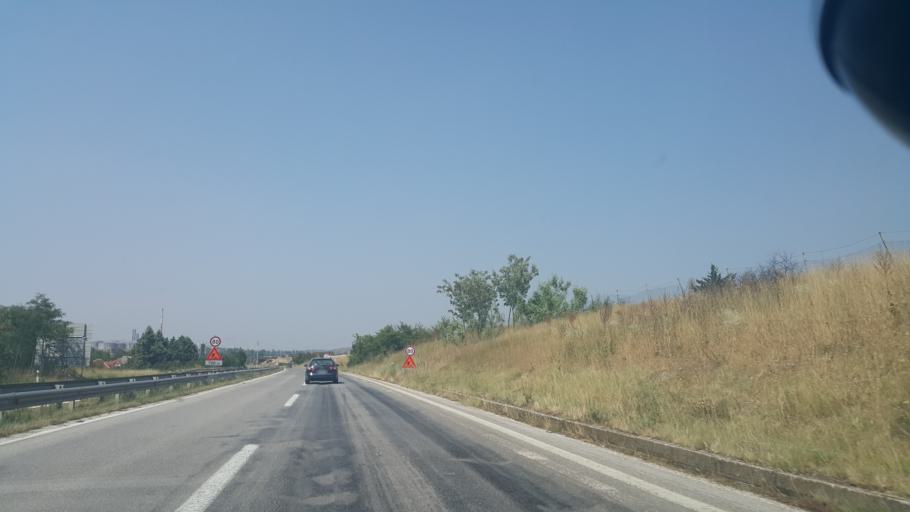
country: MK
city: Miladinovci
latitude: 41.9774
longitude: 21.6515
